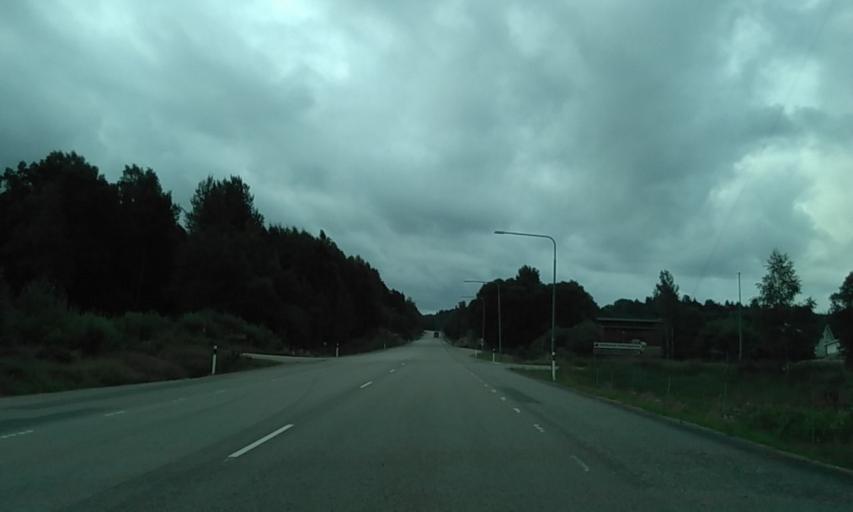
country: SE
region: Vaestra Goetaland
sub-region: Alingsas Kommun
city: Alingsas
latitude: 57.8955
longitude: 12.5492
